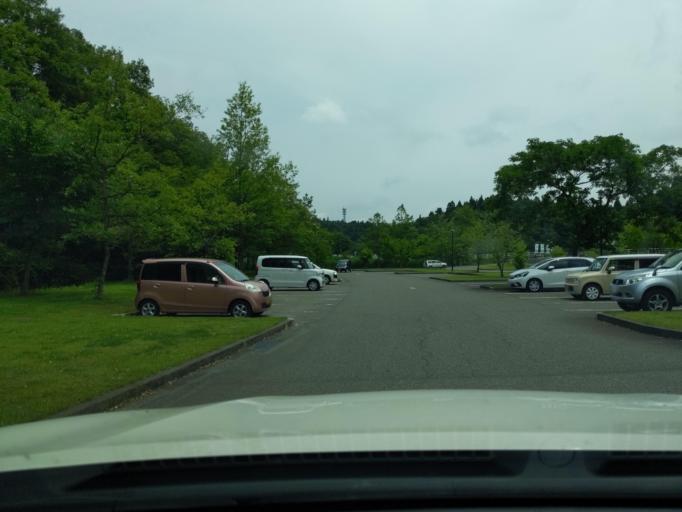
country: JP
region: Niigata
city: Kashiwazaki
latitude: 37.3327
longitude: 138.5900
